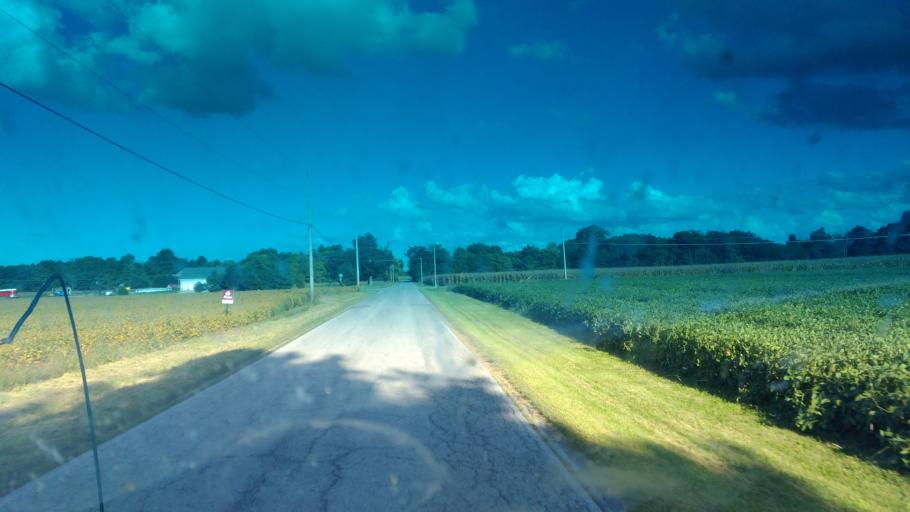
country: US
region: Ohio
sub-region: Hancock County
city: Arlington
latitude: 40.9360
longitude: -83.6759
